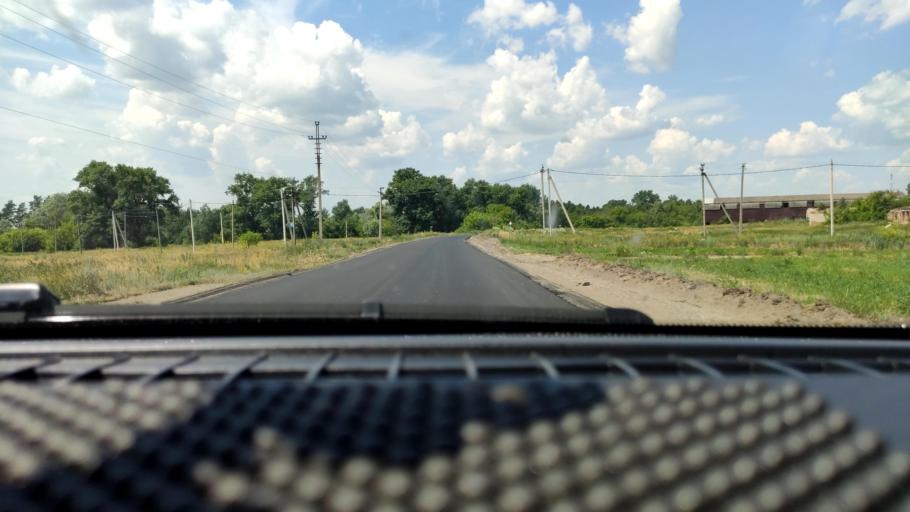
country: RU
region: Voronezj
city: Podkletnoye
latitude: 51.6144
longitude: 39.5748
